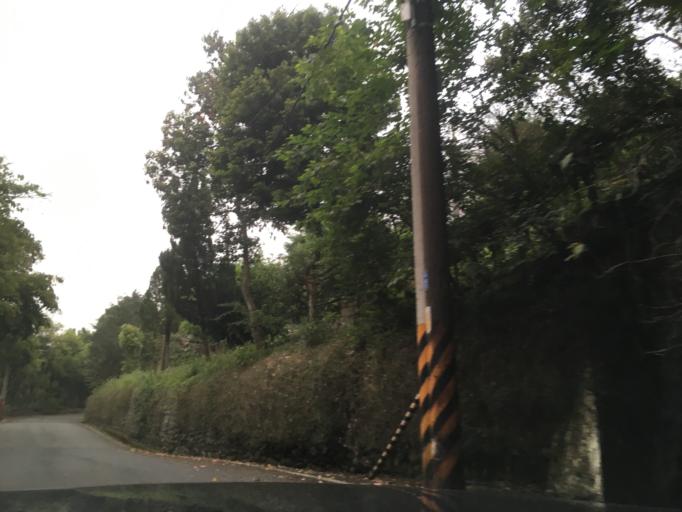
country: TW
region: Taiwan
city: Daxi
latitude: 24.8954
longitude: 121.3800
